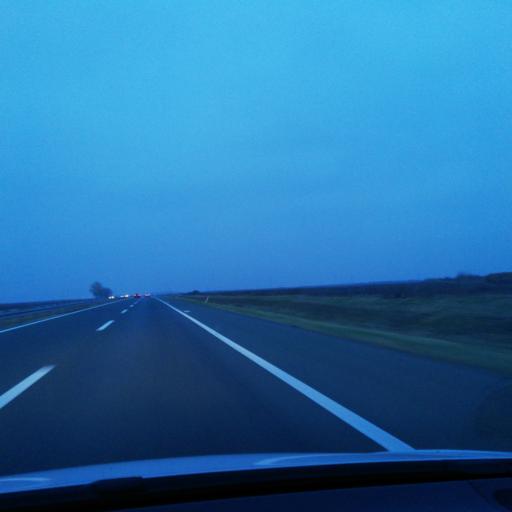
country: RS
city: Sasinci
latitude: 44.9721
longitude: 19.7613
